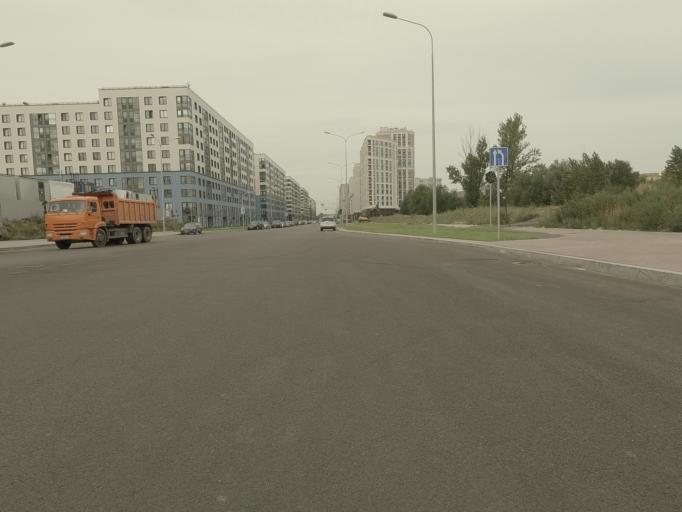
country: RU
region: St.-Petersburg
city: Admiralteisky
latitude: 59.8968
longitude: 30.3123
